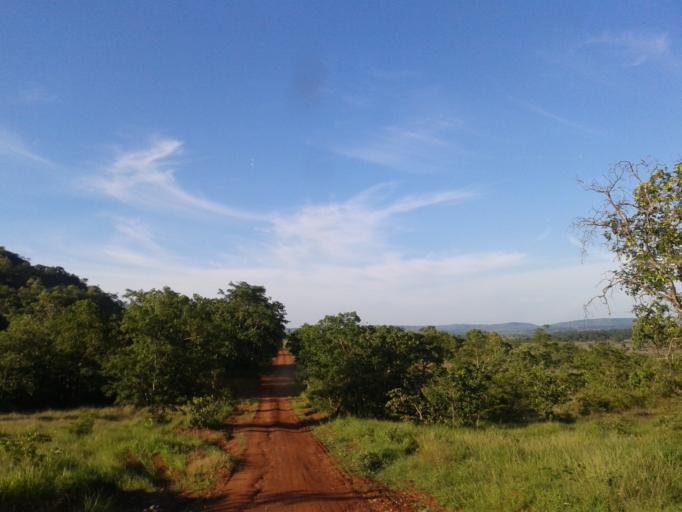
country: BR
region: Minas Gerais
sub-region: Santa Vitoria
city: Santa Vitoria
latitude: -18.9791
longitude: -49.8930
